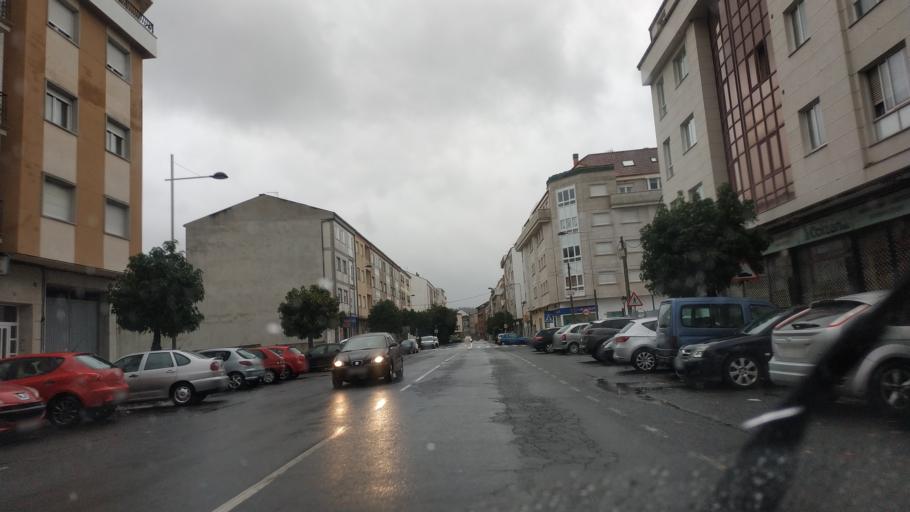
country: ES
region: Galicia
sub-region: Provincia da Coruna
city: Negreira
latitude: 42.9138
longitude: -8.7359
